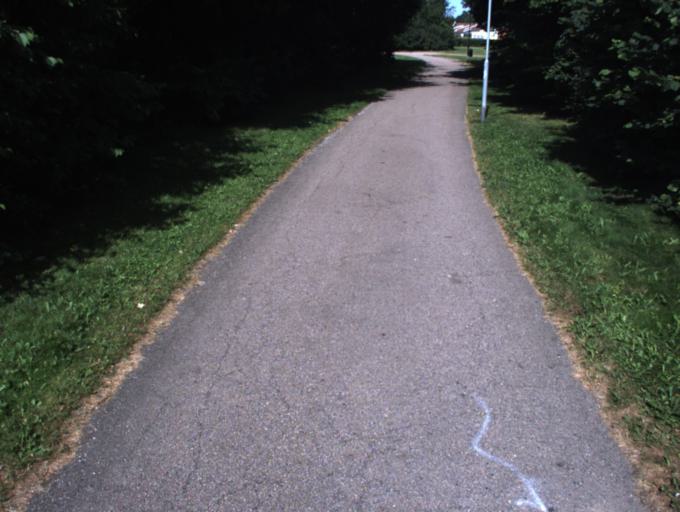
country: SE
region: Skane
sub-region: Helsingborg
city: Barslov
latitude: 56.0109
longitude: 12.8028
